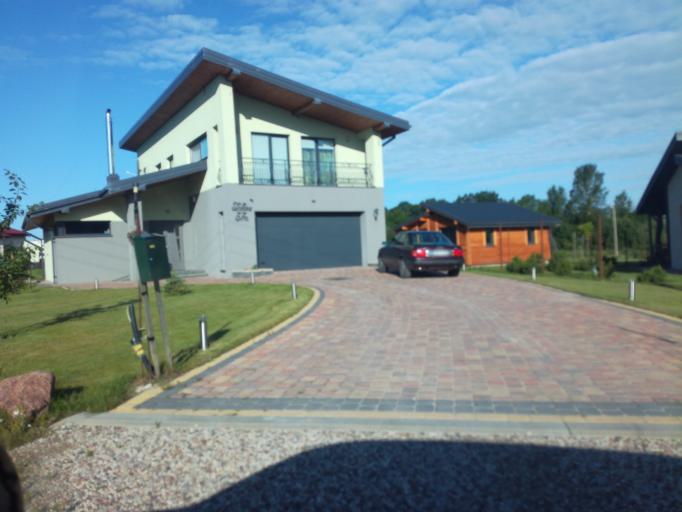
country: LT
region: Alytaus apskritis
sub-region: Alytus
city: Alytus
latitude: 54.4041
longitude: 23.9963
